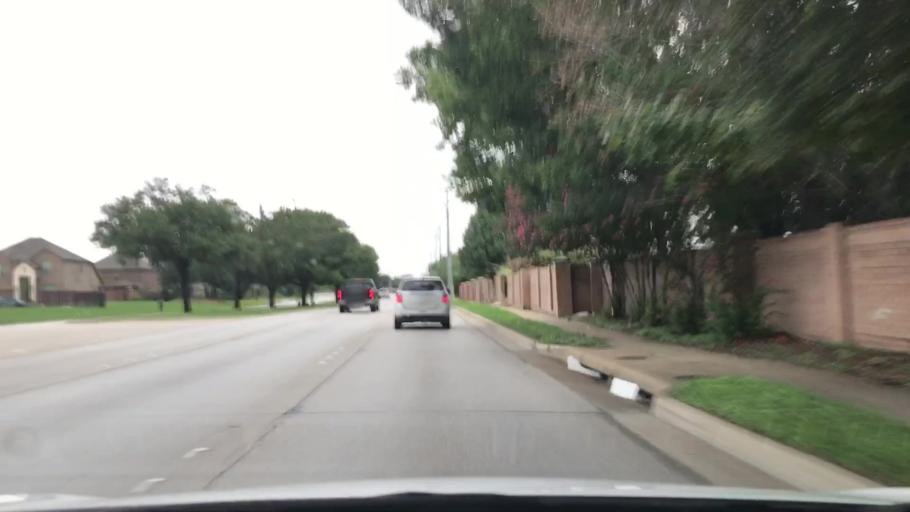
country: US
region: Texas
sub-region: Tarrant County
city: Watauga
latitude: 32.8511
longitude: -97.2899
